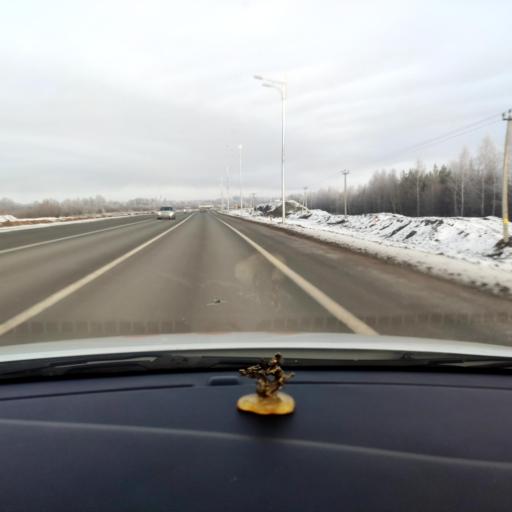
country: RU
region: Tatarstan
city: Stolbishchi
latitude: 55.6381
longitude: 49.2918
